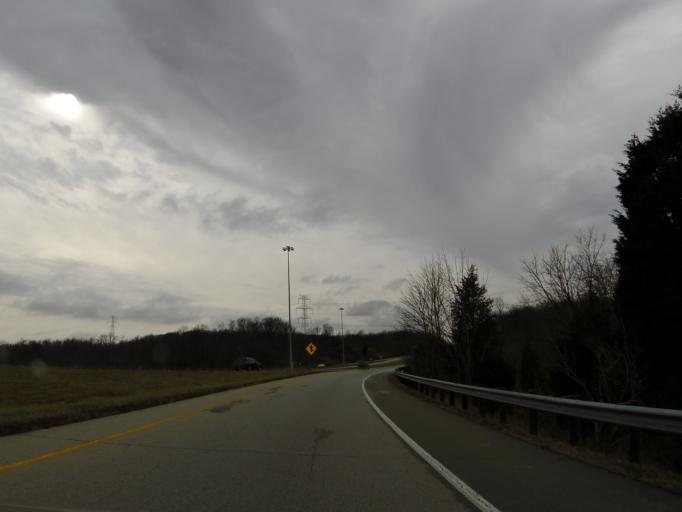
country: US
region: Ohio
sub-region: Hamilton County
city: Grandview
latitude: 39.2185
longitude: -84.7432
